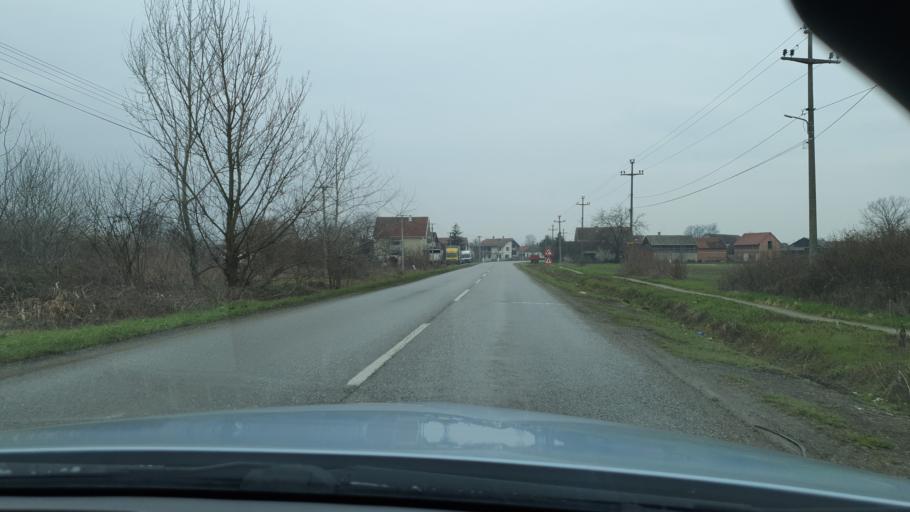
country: RS
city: Stitar
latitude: 44.7822
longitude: 19.6019
